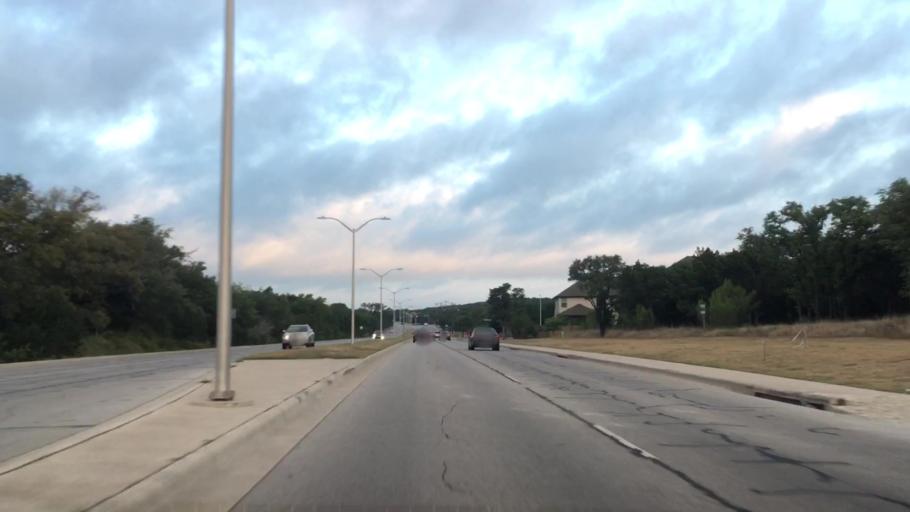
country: US
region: Texas
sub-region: Williamson County
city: Cedar Park
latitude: 30.5073
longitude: -97.7809
